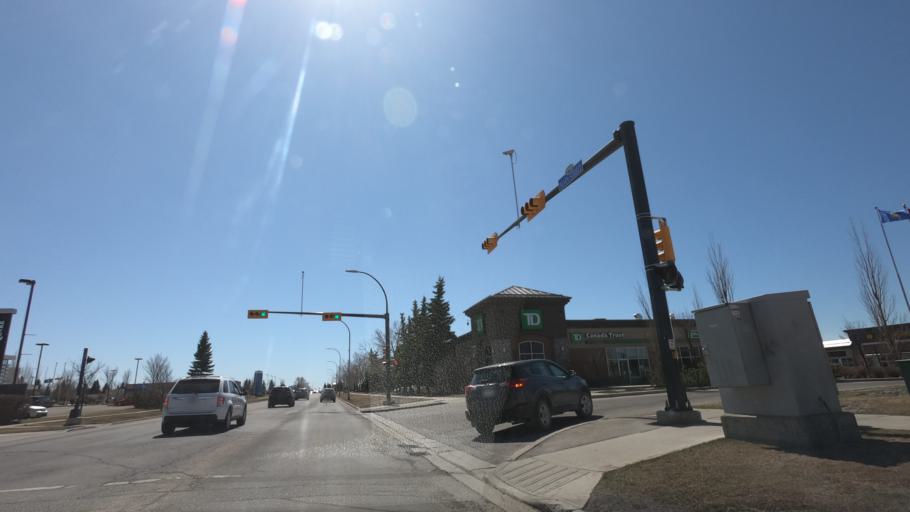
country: CA
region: Alberta
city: Airdrie
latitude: 51.2894
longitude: -114.0135
